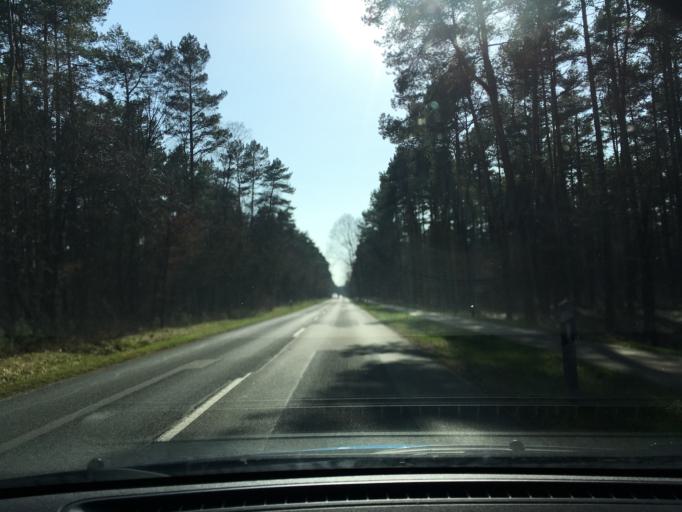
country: DE
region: Lower Saxony
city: Hambuhren
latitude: 52.6821
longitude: 9.9668
